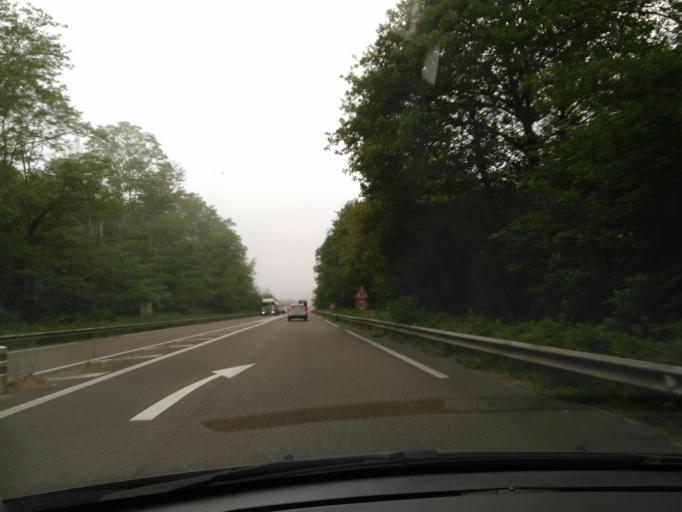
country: FR
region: Aquitaine
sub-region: Departement des Landes
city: Tartas
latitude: 43.8265
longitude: -0.8269
